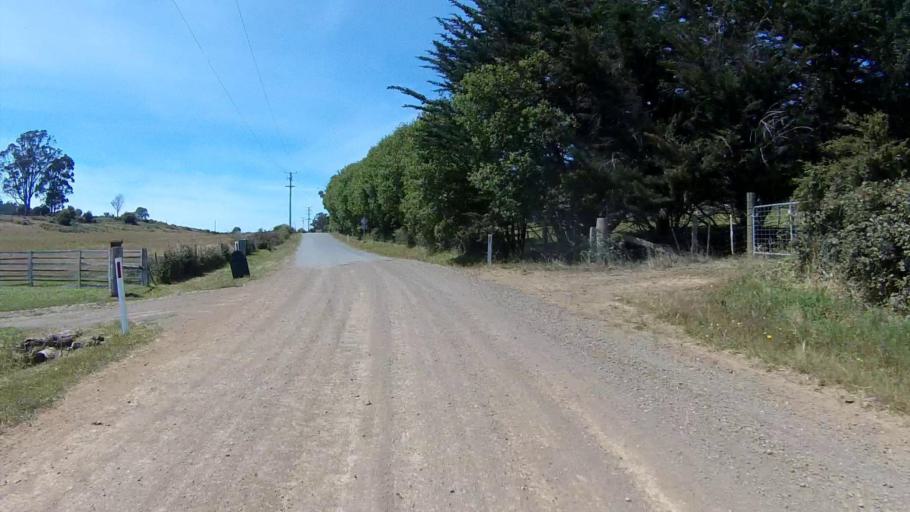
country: AU
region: Tasmania
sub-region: Sorell
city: Sorell
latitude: -42.7047
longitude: 147.7432
